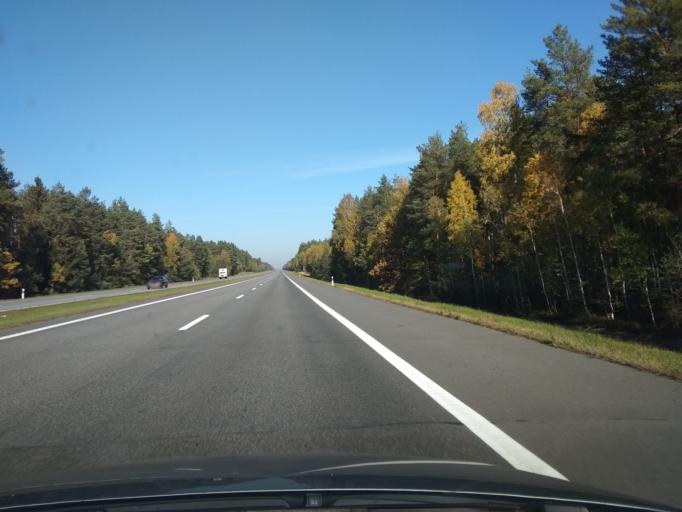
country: BY
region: Grodnenskaya
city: Zhyrovichy
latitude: 52.8707
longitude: 25.6578
